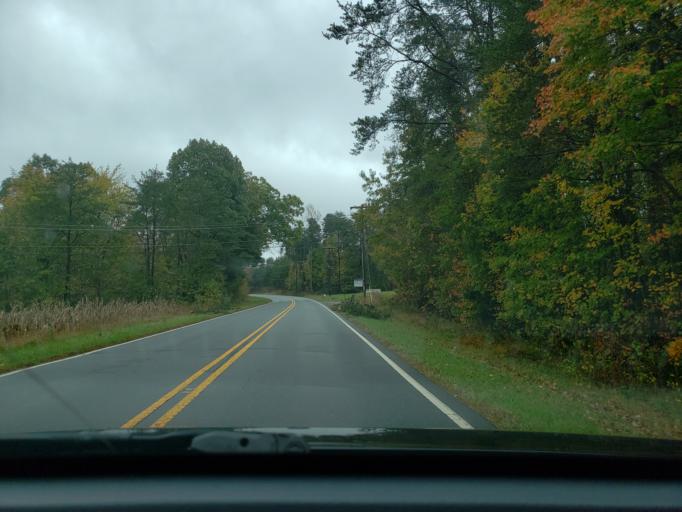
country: US
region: North Carolina
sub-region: Stokes County
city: Walnut Cove
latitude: 36.3444
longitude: -80.1536
